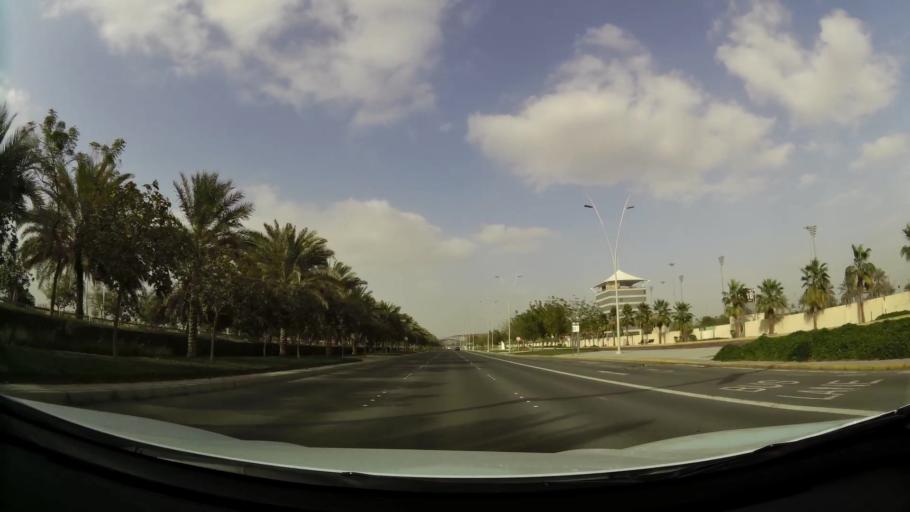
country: AE
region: Abu Dhabi
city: Abu Dhabi
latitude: 24.4712
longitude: 54.6010
